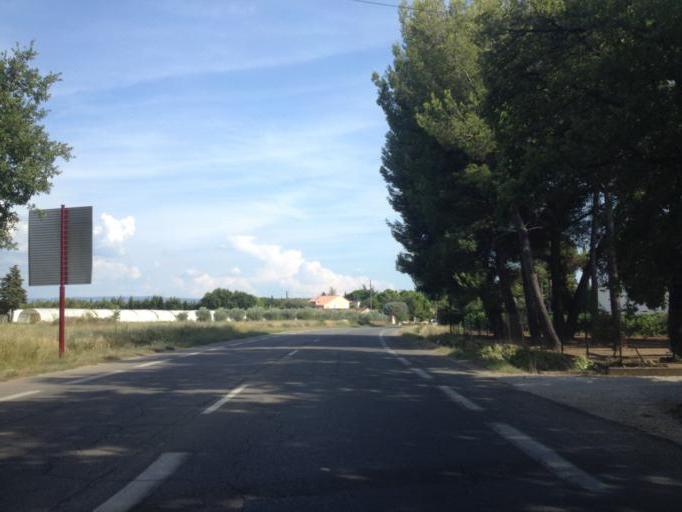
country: FR
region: Provence-Alpes-Cote d'Azur
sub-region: Departement du Vaucluse
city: Aubignan
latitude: 44.0803
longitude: 5.0392
